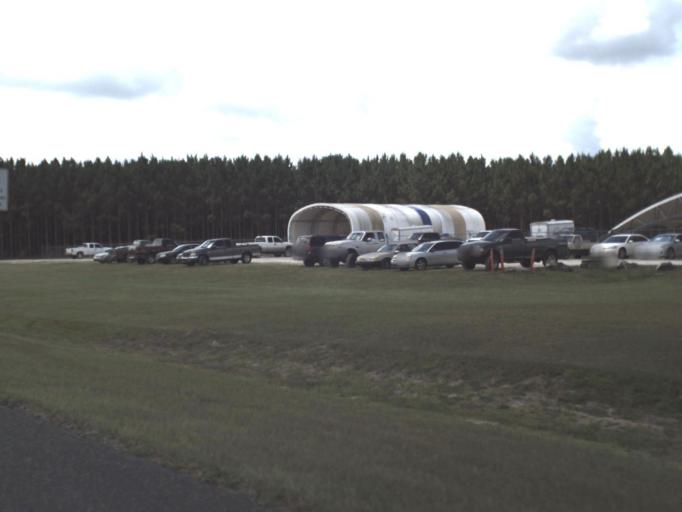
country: US
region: Florida
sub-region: Taylor County
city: Perry
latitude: 30.1608
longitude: -83.6229
